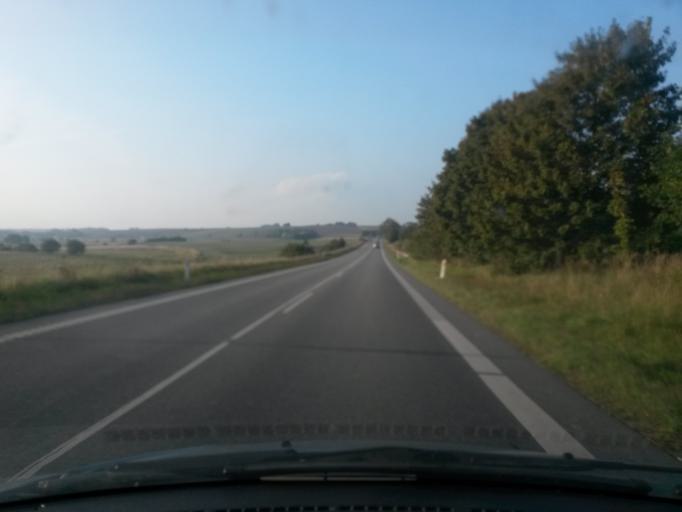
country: DK
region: Central Jutland
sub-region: Syddjurs Kommune
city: Hornslet
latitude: 56.3661
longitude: 10.3240
